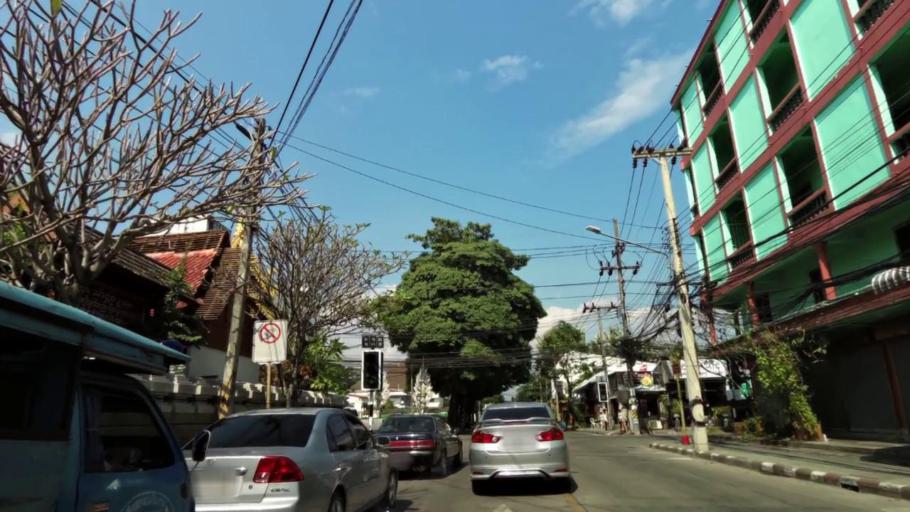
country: TH
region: Chiang Rai
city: Chiang Rai
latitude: 19.9109
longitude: 99.8327
